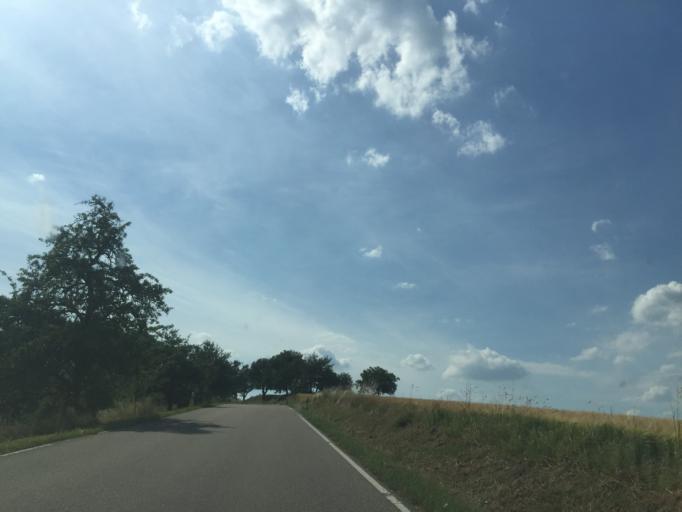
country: DE
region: Baden-Wuerttemberg
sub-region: Karlsruhe Region
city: Zuzenhausen
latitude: 49.2738
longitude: 8.8330
